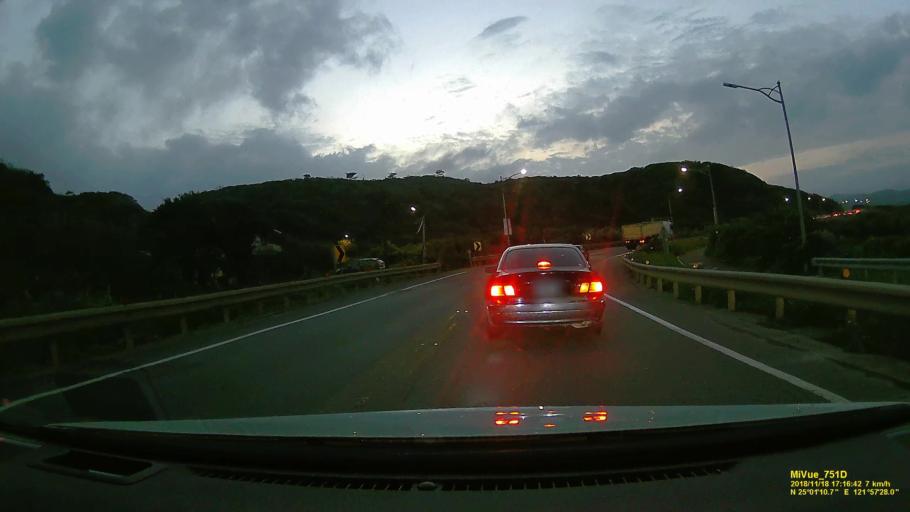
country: TW
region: Taiwan
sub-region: Keelung
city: Keelung
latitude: 25.0196
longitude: 121.9578
